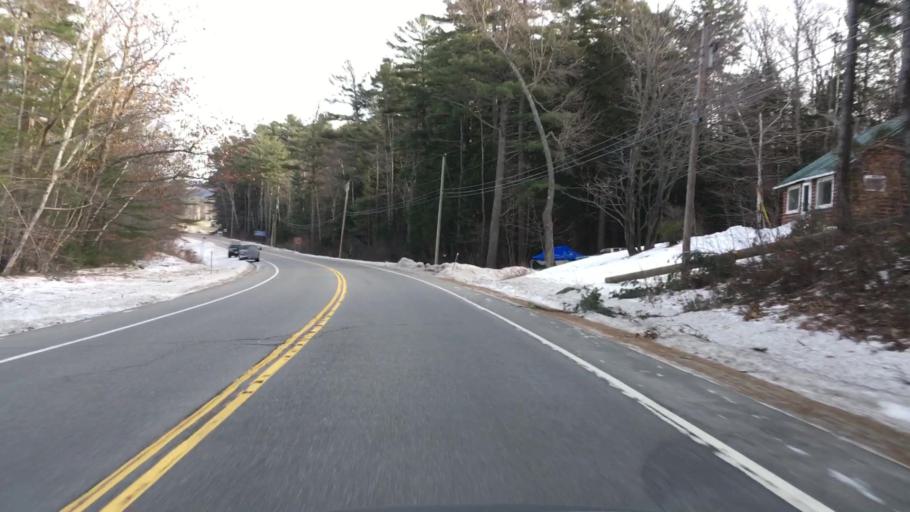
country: US
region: New Hampshire
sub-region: Sullivan County
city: Sunapee
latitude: 43.3416
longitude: -72.0803
